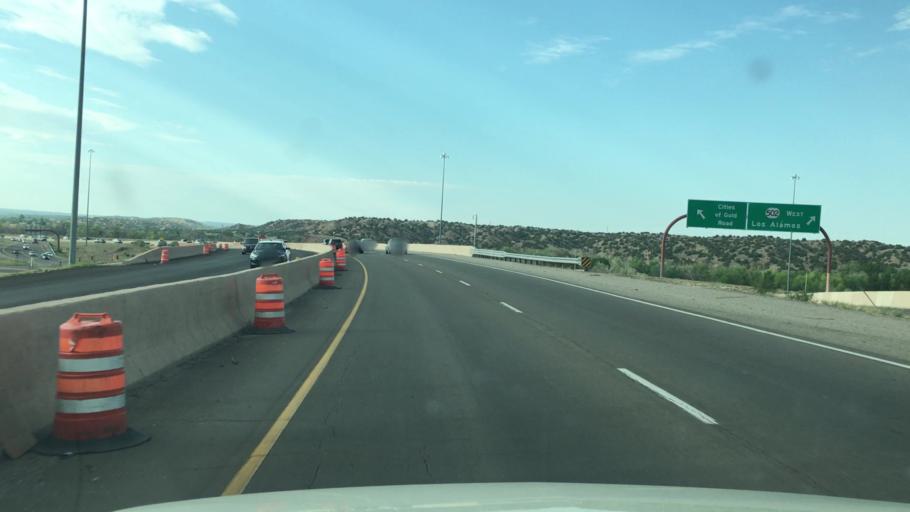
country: US
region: New Mexico
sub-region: Santa Fe County
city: Pojoaque
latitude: 35.8924
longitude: -106.0231
